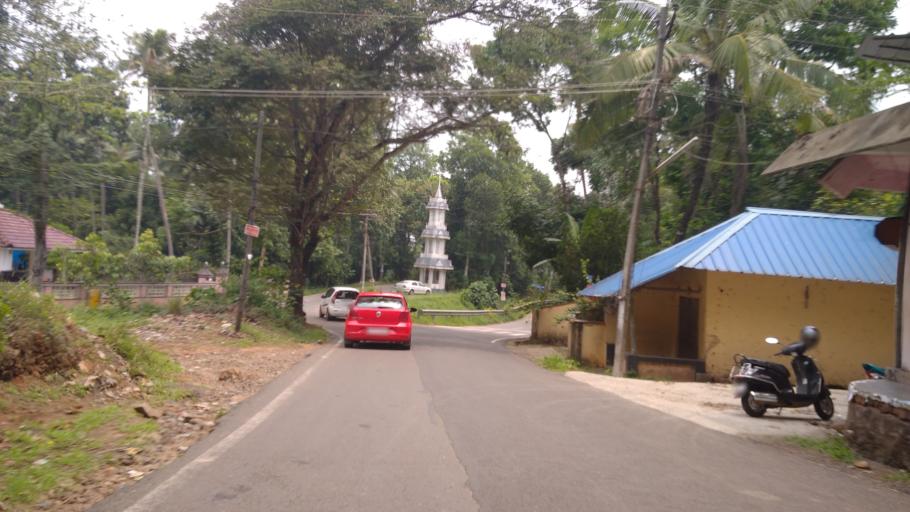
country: IN
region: Kerala
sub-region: Ernakulam
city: Ramamangalam
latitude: 10.0123
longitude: 76.4846
